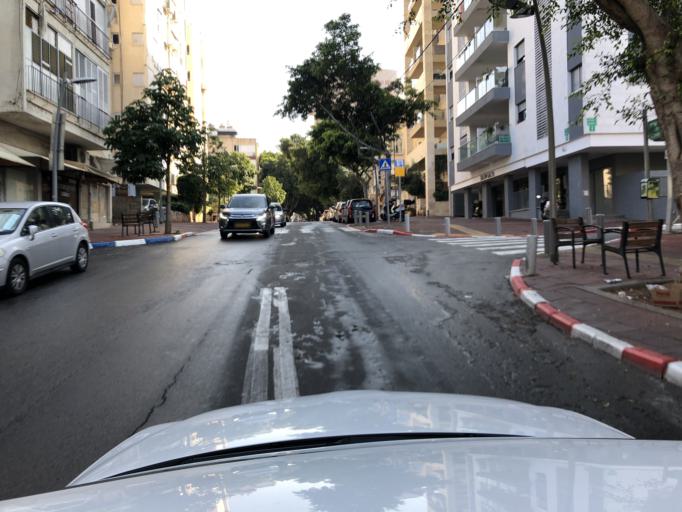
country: IL
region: Tel Aviv
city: Ramat Gan
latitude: 32.0928
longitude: 34.8177
